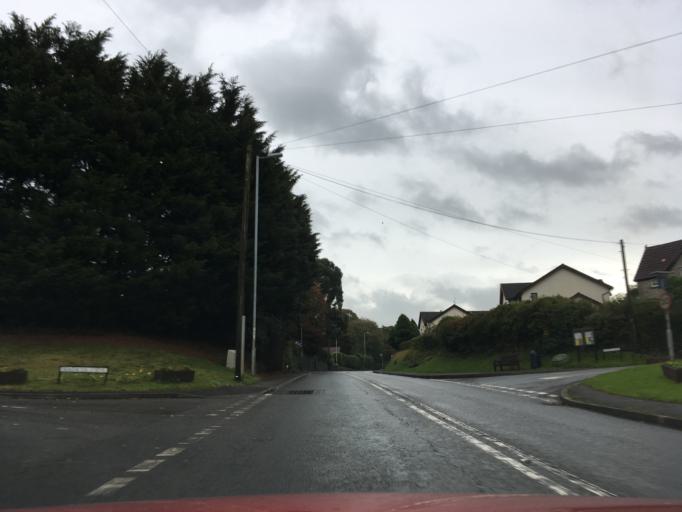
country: GB
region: Wales
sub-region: Monmouthshire
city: Chepstow
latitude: 51.6293
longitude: -2.6966
